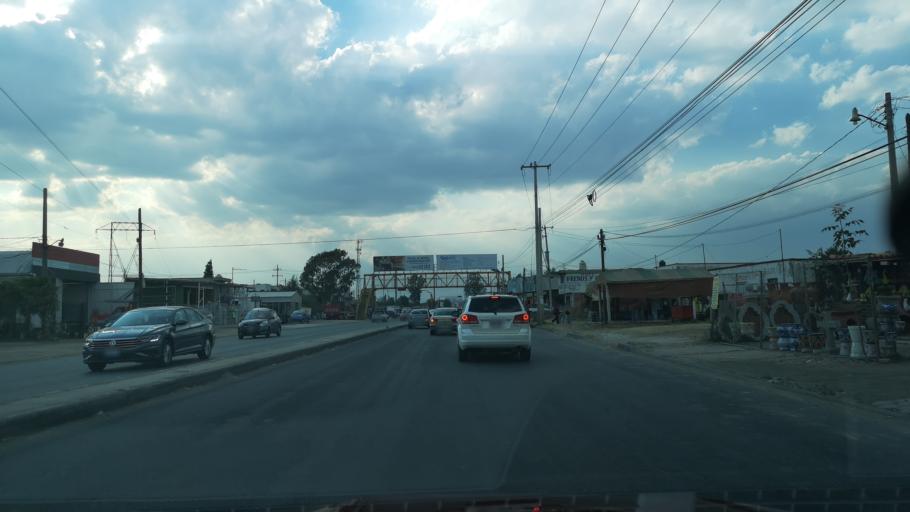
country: MX
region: Puebla
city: Cholula
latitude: 19.0776
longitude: -98.3238
